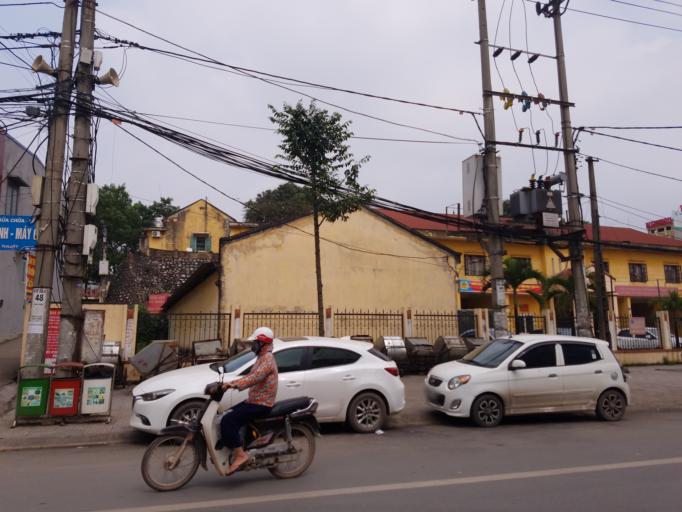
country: VN
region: Thai Nguyen
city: Thanh Pho Thai Nguyen
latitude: 21.5941
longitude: 105.8248
